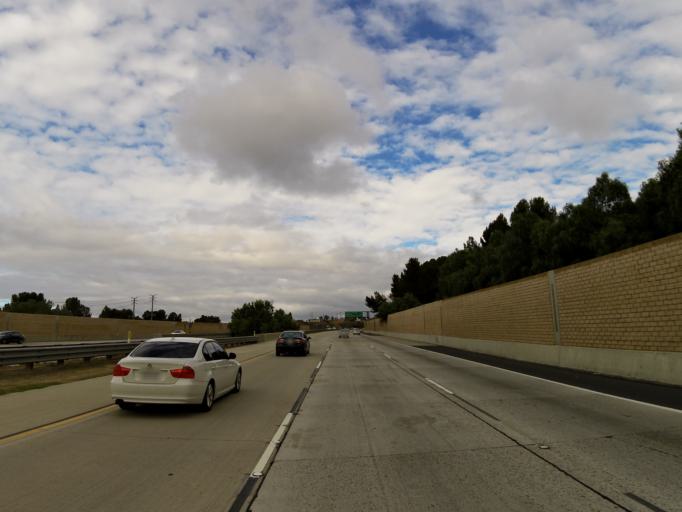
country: US
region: California
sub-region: Ventura County
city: Thousand Oaks
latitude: 34.2174
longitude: -118.8494
